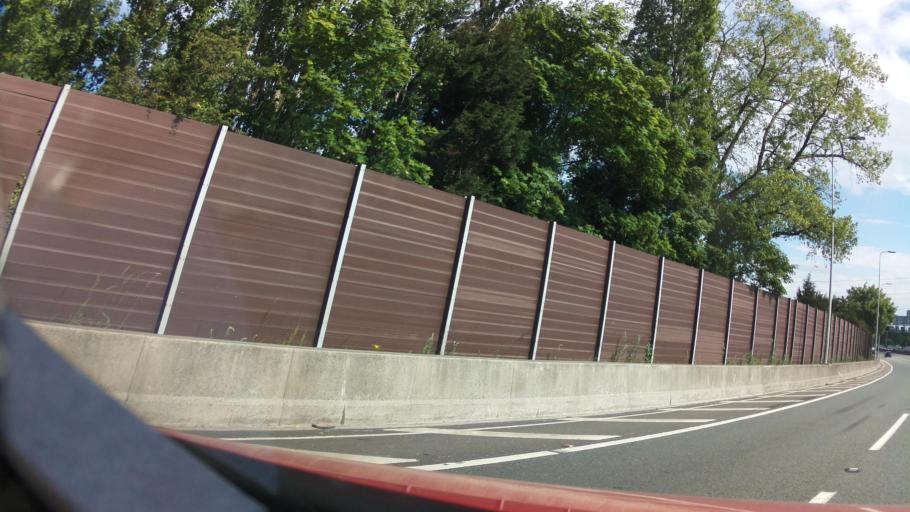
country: GB
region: England
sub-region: City and Borough of Salford
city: Walkden
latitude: 53.4969
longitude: -2.3845
